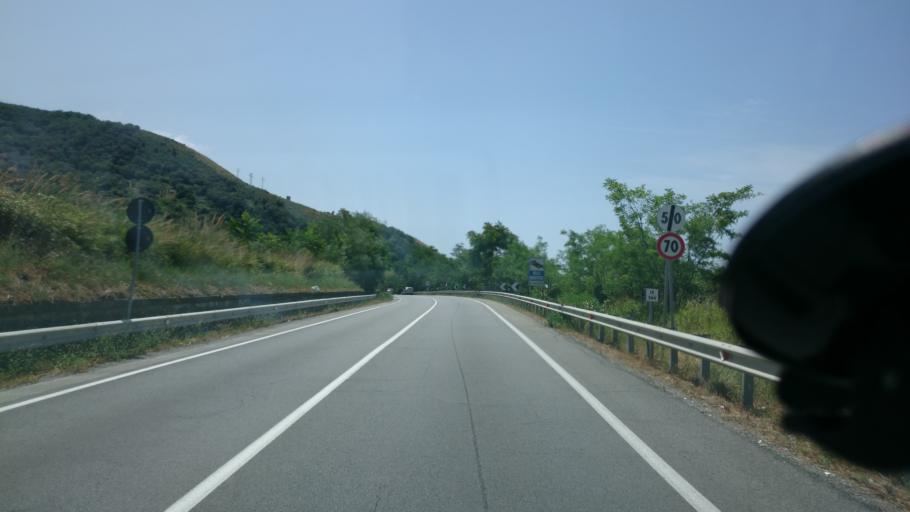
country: IT
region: Calabria
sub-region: Provincia di Cosenza
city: Cittadella del Capo
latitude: 39.5911
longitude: 15.8682
